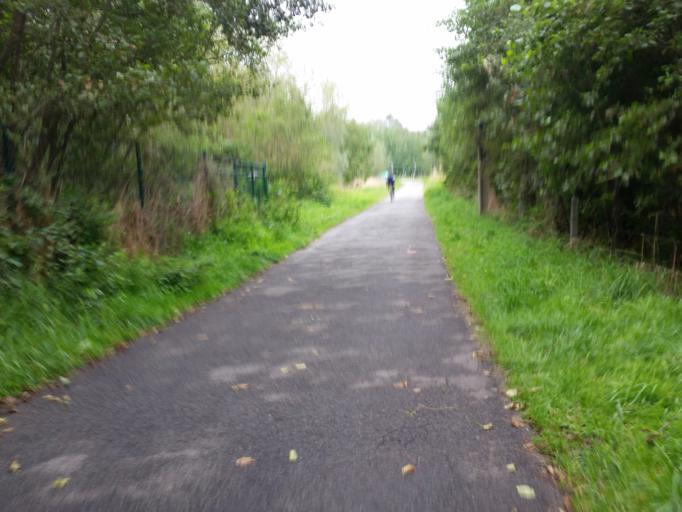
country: BE
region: Flanders
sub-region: Provincie Antwerpen
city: Kontich
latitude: 51.1245
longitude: 4.4465
